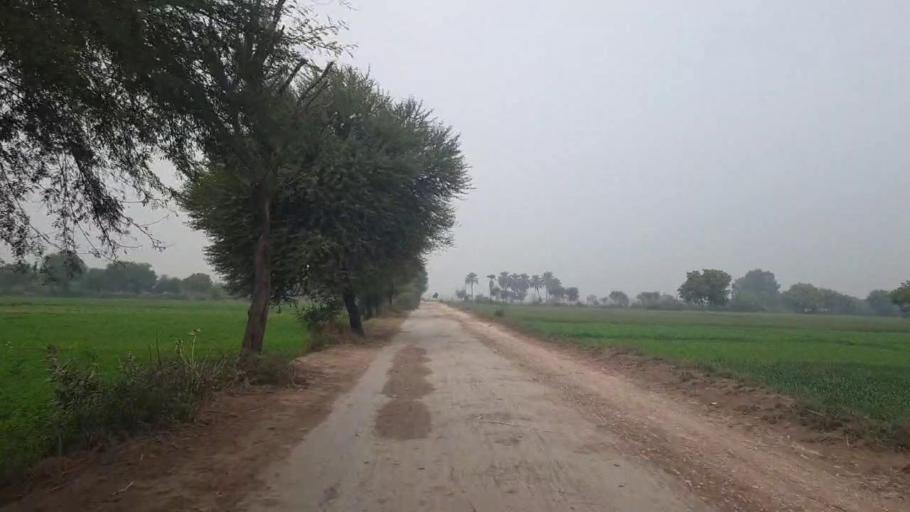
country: PK
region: Sindh
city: Tando Adam
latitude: 25.7686
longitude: 68.7025
